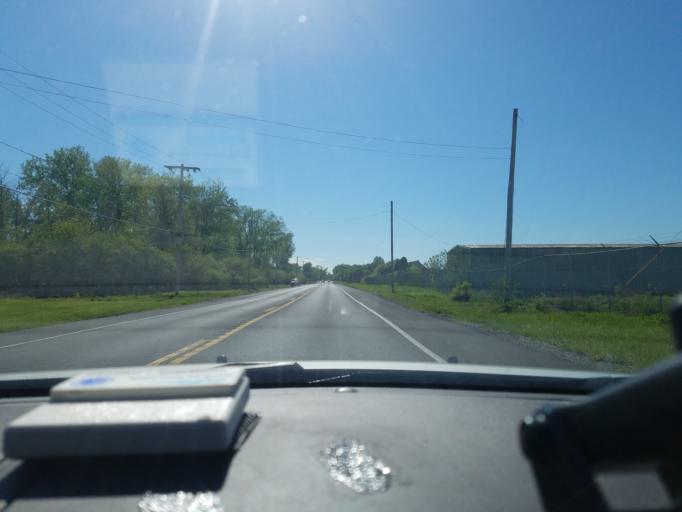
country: US
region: New York
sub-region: Onondaga County
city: Mattydale
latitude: 43.1053
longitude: -76.1271
